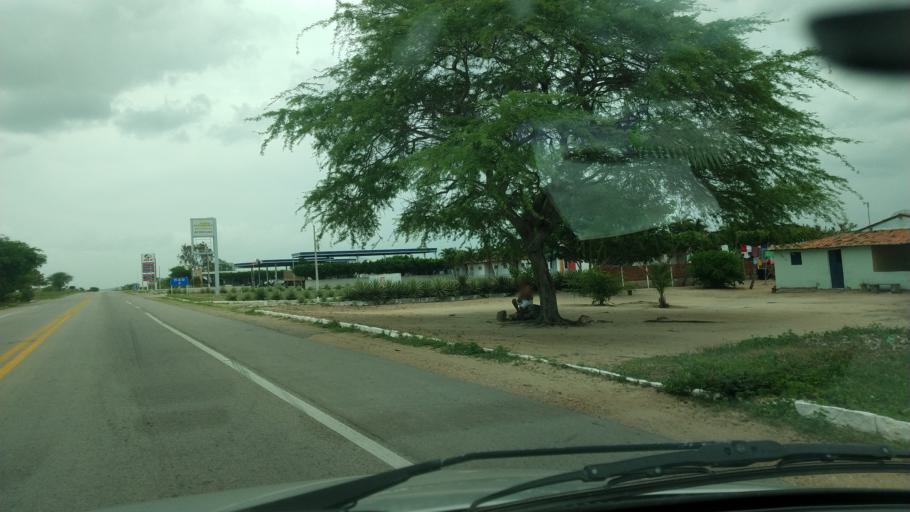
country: BR
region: Rio Grande do Norte
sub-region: Tangara
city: Tangara
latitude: -6.1722
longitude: -35.7636
